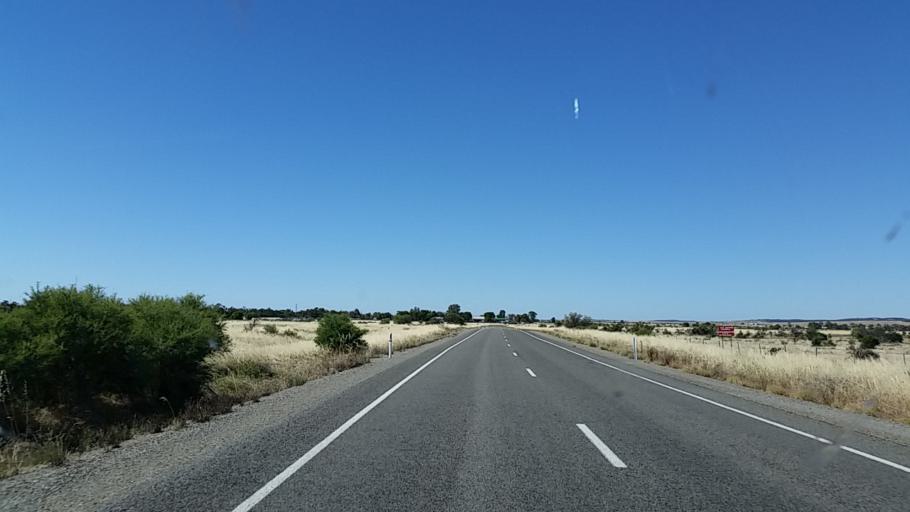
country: AU
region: South Australia
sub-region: Peterborough
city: Peterborough
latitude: -33.1598
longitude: 138.9182
